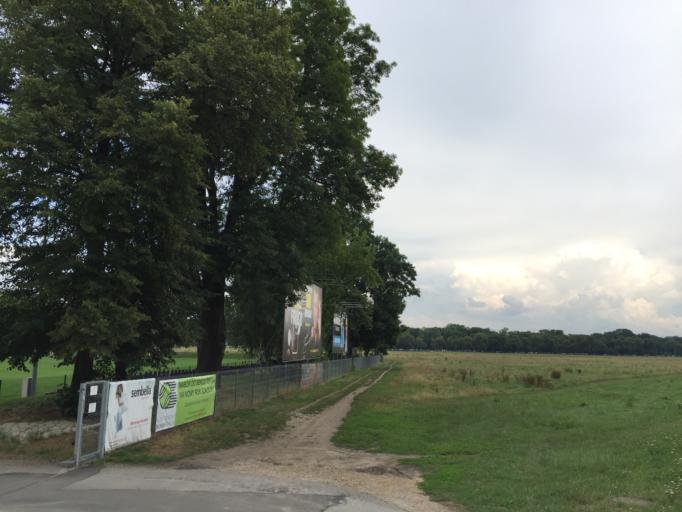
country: PL
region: Lesser Poland Voivodeship
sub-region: Krakow
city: Krakow
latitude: 50.0571
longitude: 19.9077
